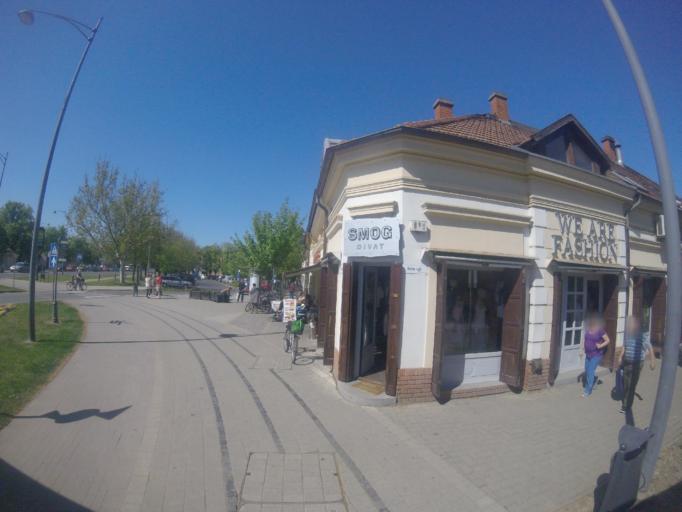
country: HU
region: Bekes
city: Gyula
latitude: 46.6441
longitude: 21.2720
